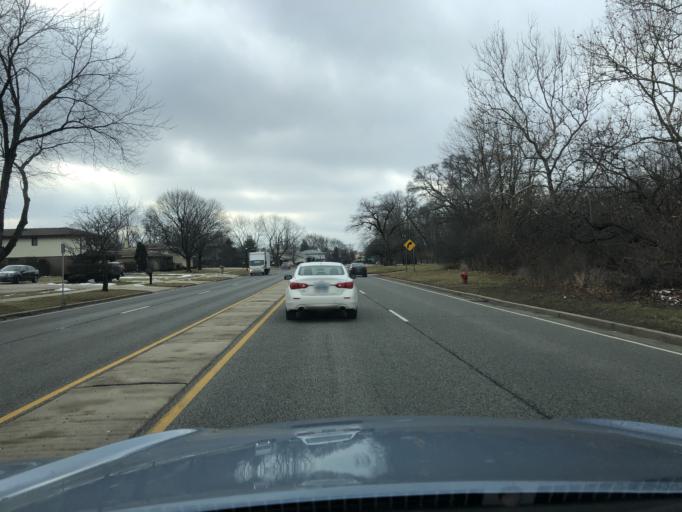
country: US
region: Illinois
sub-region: Cook County
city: Elk Grove Village
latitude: 42.0155
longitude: -87.9938
